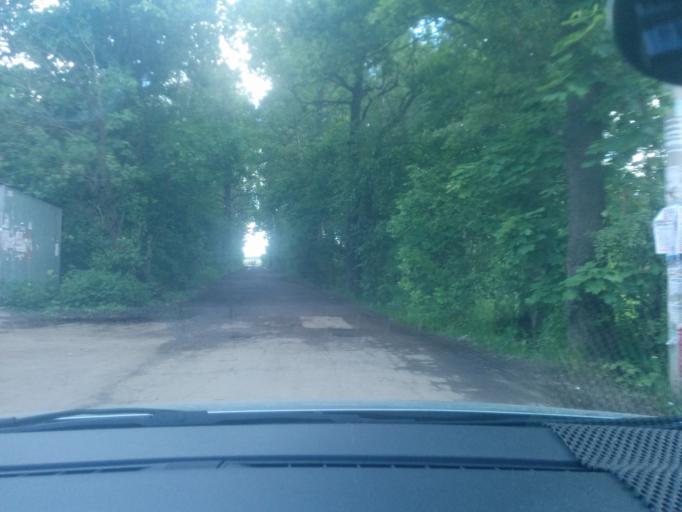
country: RU
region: Moskovskaya
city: Lugovaya
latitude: 56.0499
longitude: 37.4936
